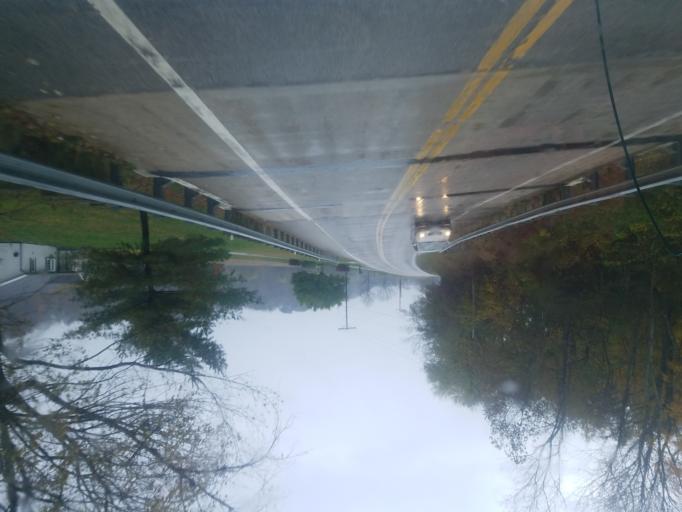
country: US
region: Ohio
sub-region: Morgan County
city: McConnelsville
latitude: 39.5755
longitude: -81.7852
